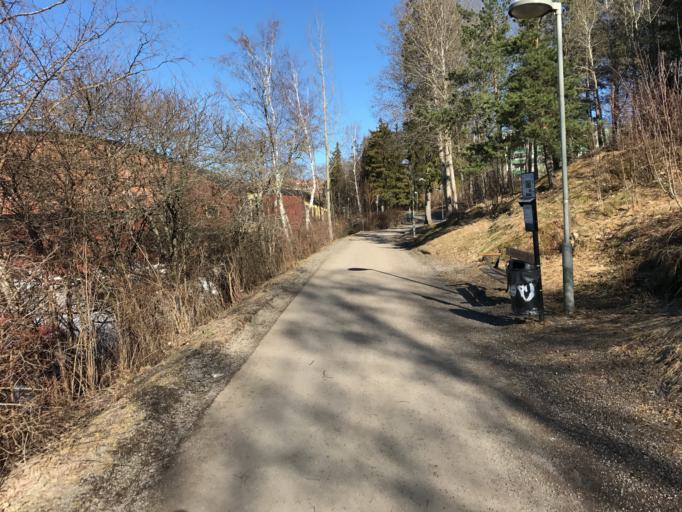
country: SE
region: Stockholm
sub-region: Stockholms Kommun
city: Kista
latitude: 59.4099
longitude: 17.9200
